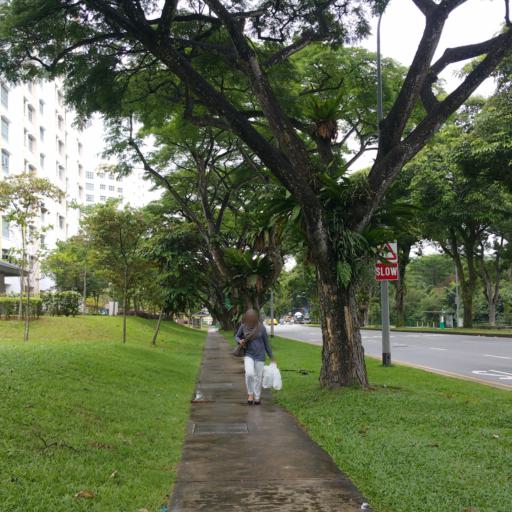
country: MY
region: Johor
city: Kampung Pasir Gudang Baru
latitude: 1.4203
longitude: 103.8482
